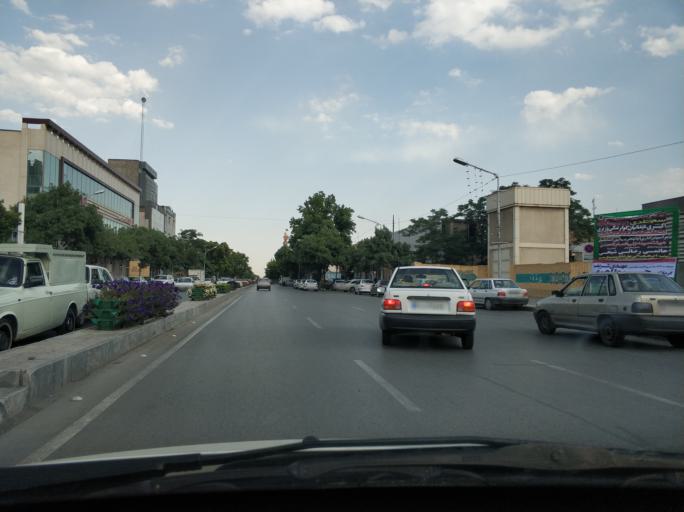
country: IR
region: Razavi Khorasan
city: Mashhad
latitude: 36.2811
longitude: 59.5960
